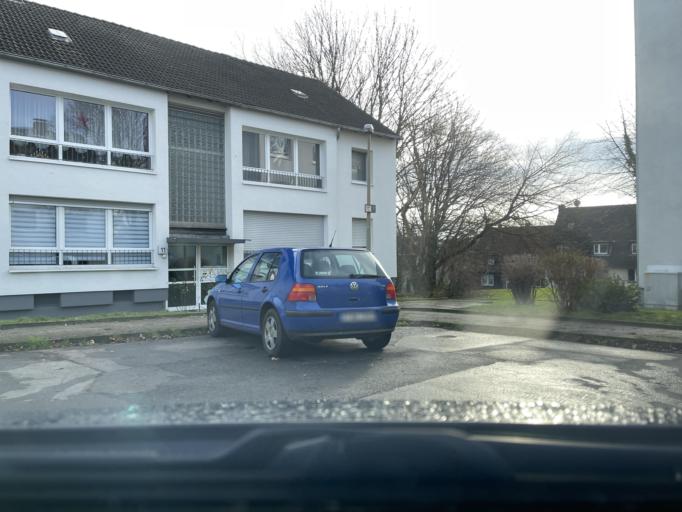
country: DE
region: North Rhine-Westphalia
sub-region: Regierungsbezirk Munster
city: Bottrop
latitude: 51.4811
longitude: 6.9350
